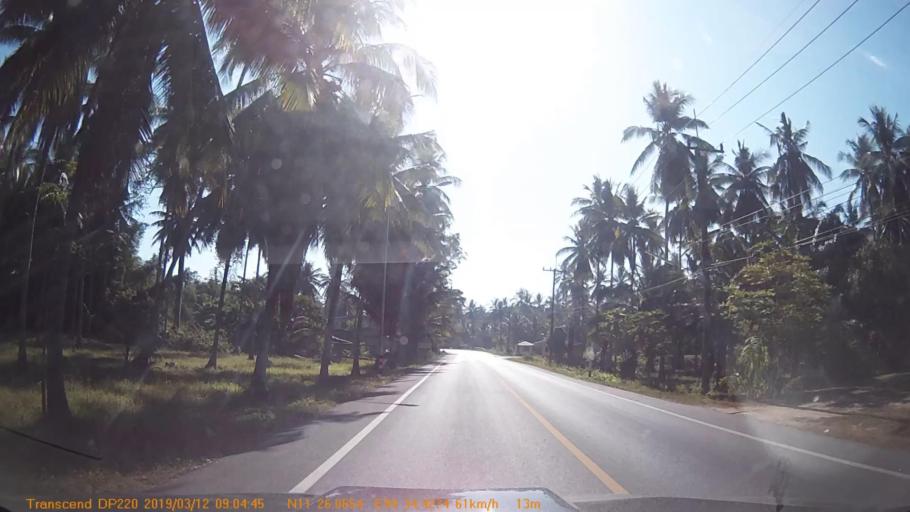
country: TH
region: Prachuap Khiri Khan
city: Thap Sakae
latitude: 11.4344
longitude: 99.5741
